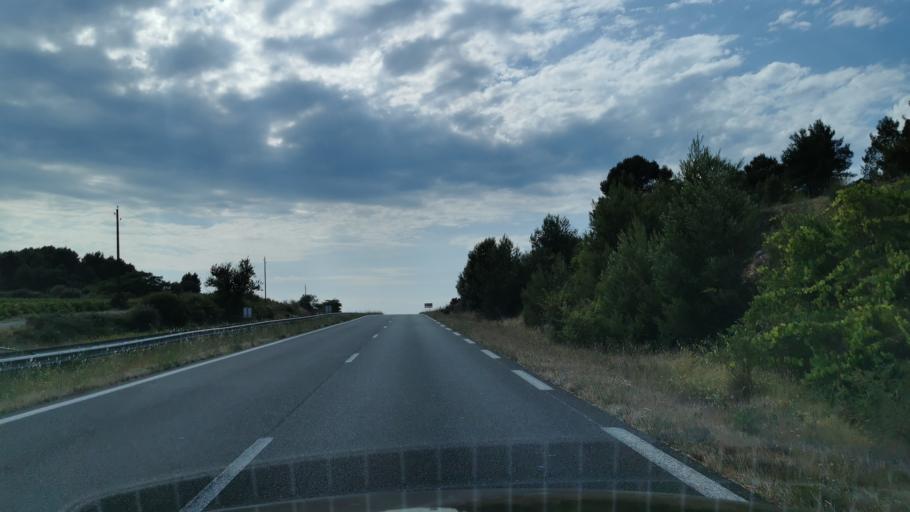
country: FR
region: Languedoc-Roussillon
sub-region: Departement de l'Herault
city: Cazouls-les-Beziers
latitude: 43.3655
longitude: 3.0828
